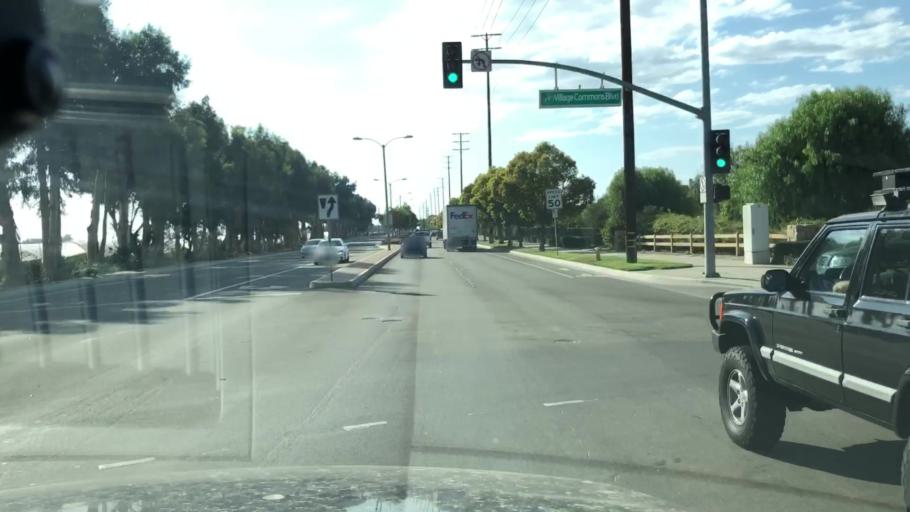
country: US
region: California
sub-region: Ventura County
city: Camarillo
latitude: 34.2055
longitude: -119.0252
